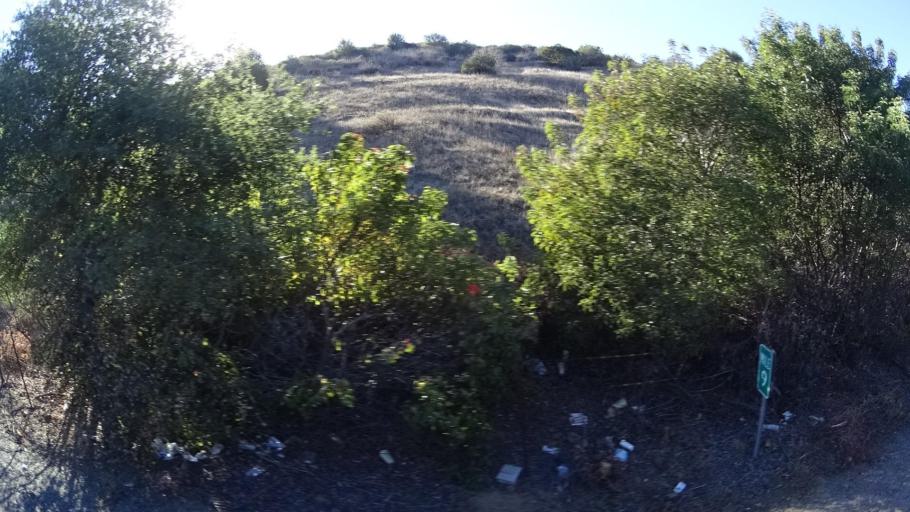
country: US
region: California
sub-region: San Diego County
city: Jamul
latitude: 32.6500
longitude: -116.8674
